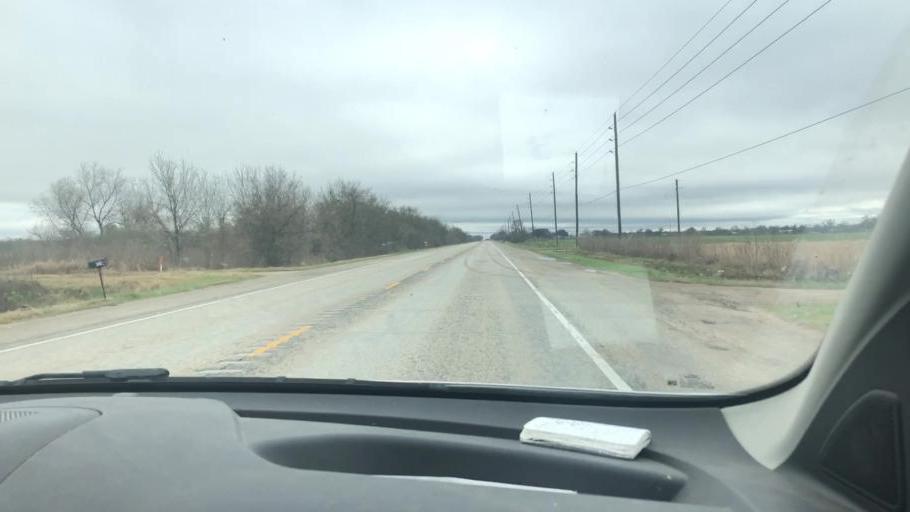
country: US
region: Texas
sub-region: Wharton County
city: Wharton
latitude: 29.2765
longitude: -96.0639
